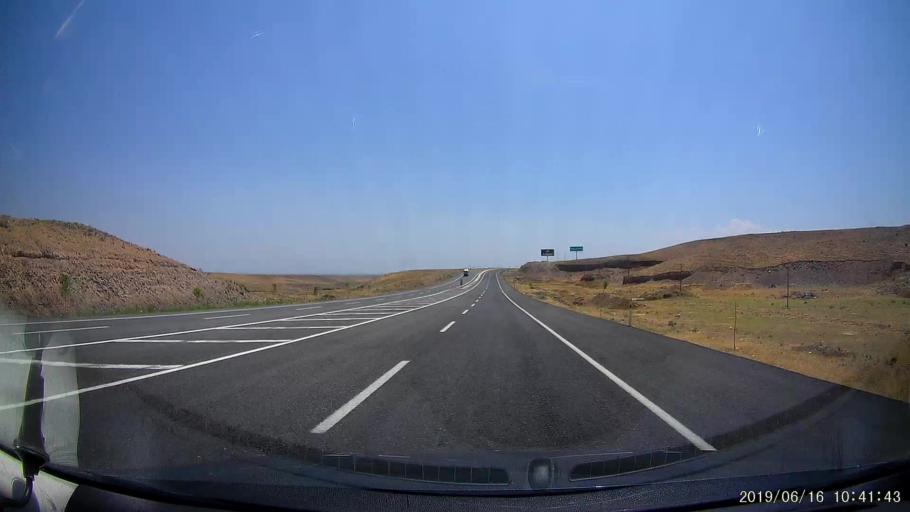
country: TR
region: Igdir
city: Tuzluca
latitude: 40.0465
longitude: 43.7899
